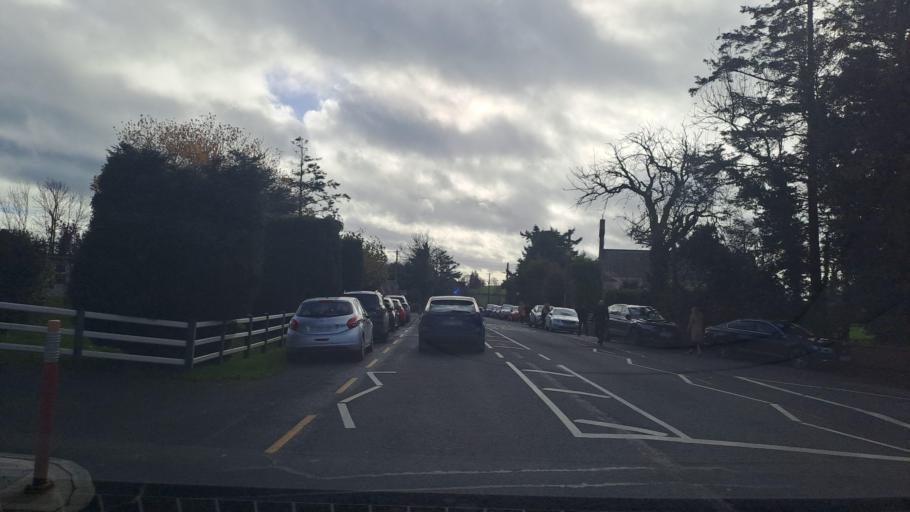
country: IE
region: Ulster
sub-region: County Monaghan
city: Monaghan
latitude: 54.1908
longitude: -6.9905
